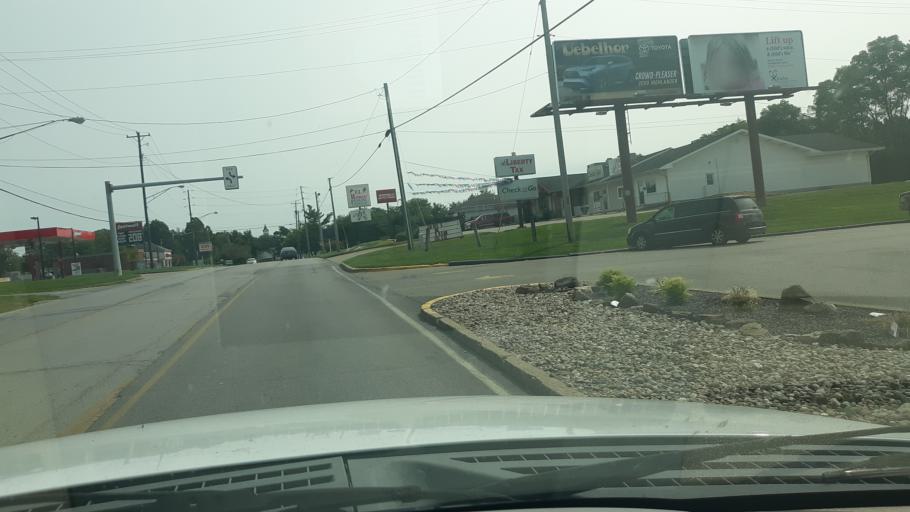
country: US
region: Indiana
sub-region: Gibson County
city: Princeton
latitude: 38.3554
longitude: -87.5814
